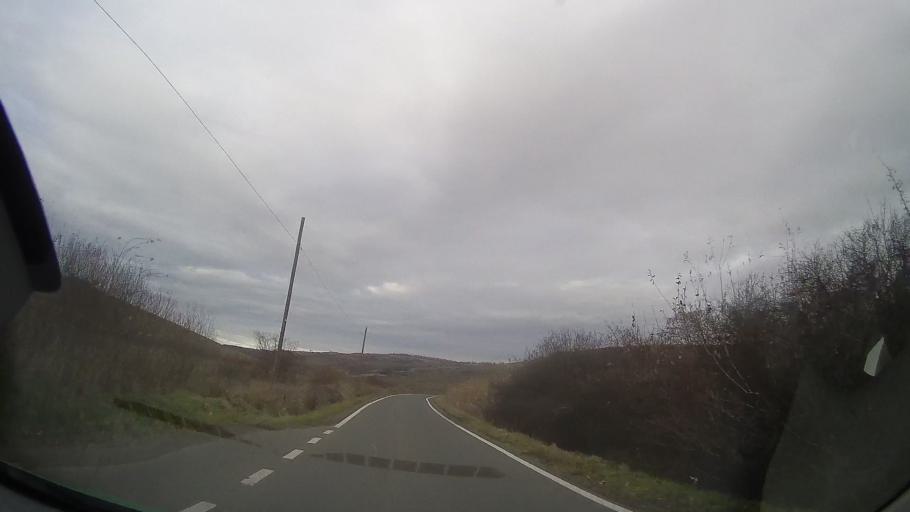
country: RO
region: Mures
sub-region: Comuna Cozma
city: Cozma
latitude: 46.7920
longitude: 24.5429
